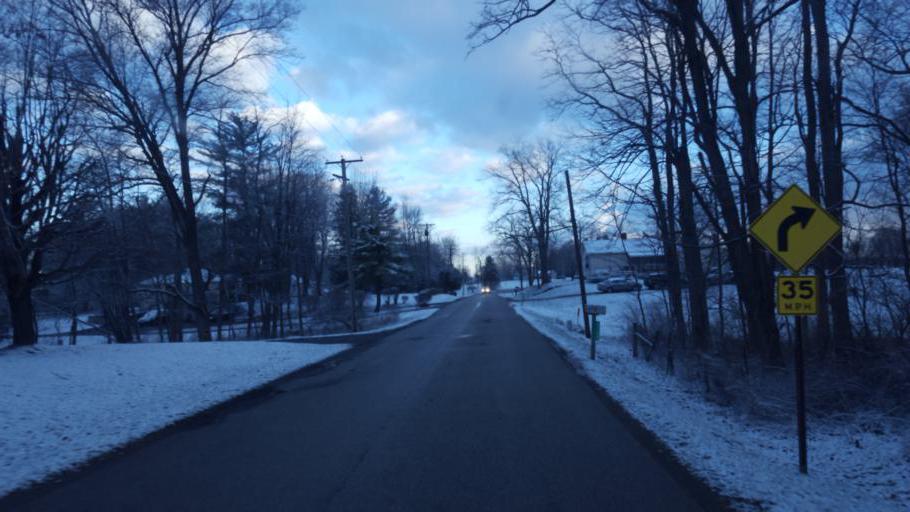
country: US
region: Ohio
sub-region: Morrow County
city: Mount Gilead
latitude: 40.5639
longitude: -82.8424
